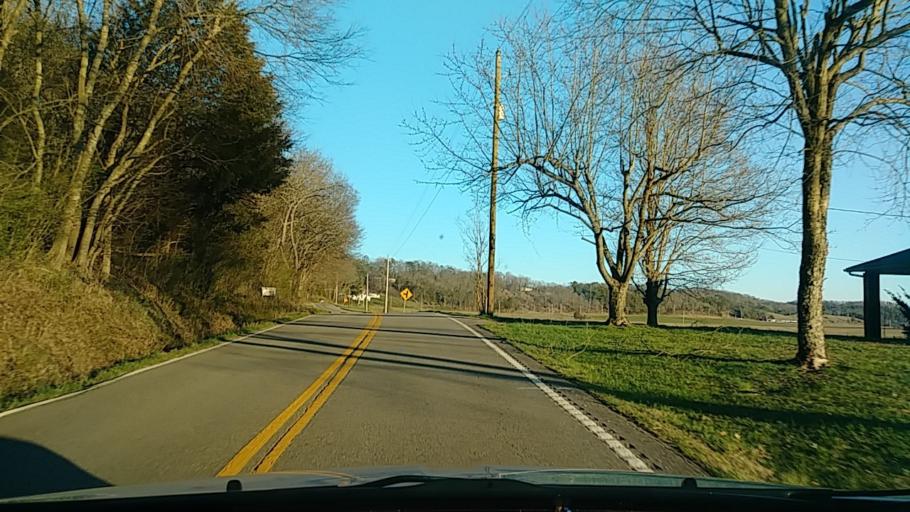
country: US
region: Tennessee
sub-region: Greene County
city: Mosheim
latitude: 36.1219
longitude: -83.0890
